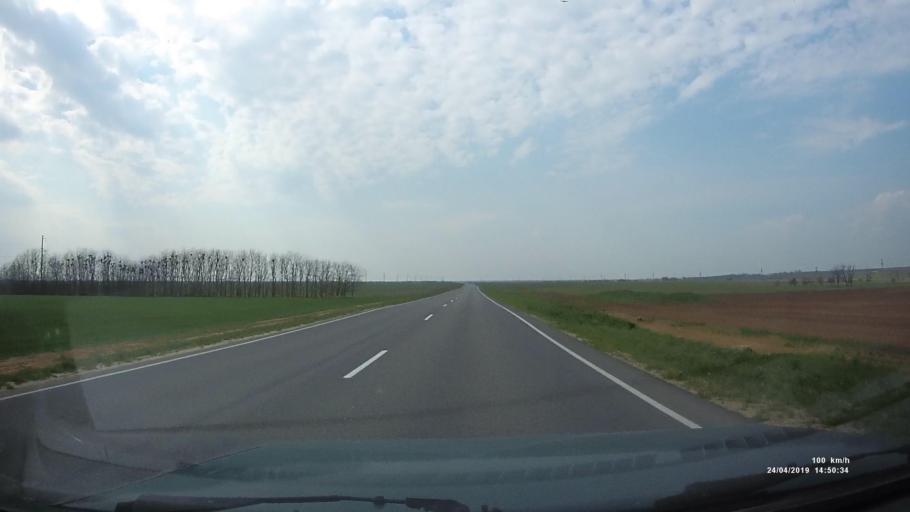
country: RU
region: Rostov
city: Remontnoye
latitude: 46.5183
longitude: 43.7170
